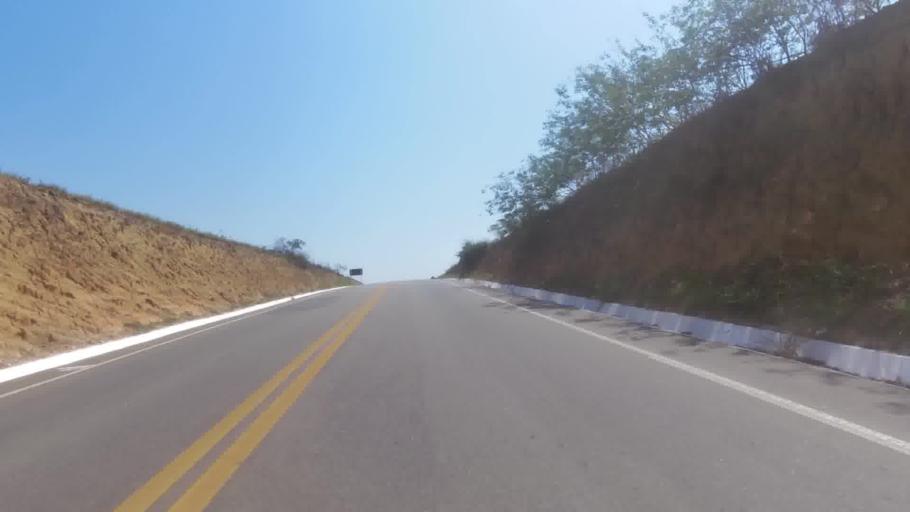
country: BR
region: Espirito Santo
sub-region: Marataizes
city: Marataizes
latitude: -21.0922
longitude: -40.8473
